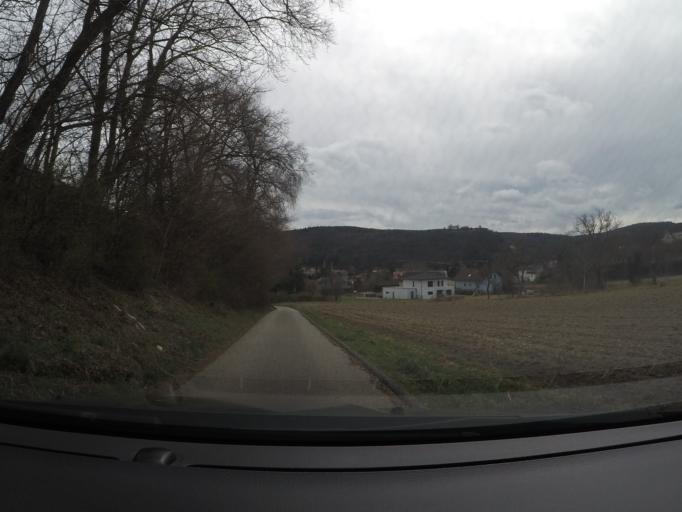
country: AT
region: Lower Austria
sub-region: Politischer Bezirk Neunkirchen
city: Pitten
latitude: 47.7272
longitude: 16.1866
